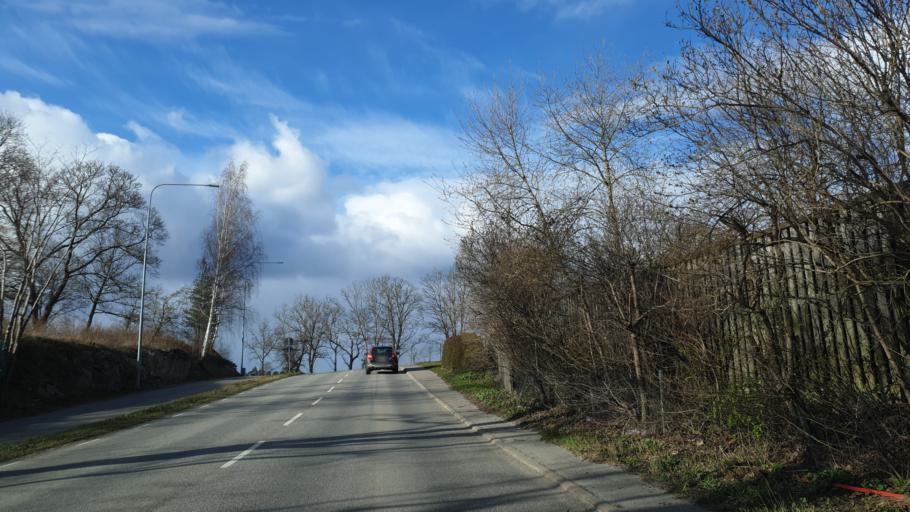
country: SE
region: Stockholm
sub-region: Lidingo
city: Lidingoe
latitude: 59.3762
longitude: 18.1282
